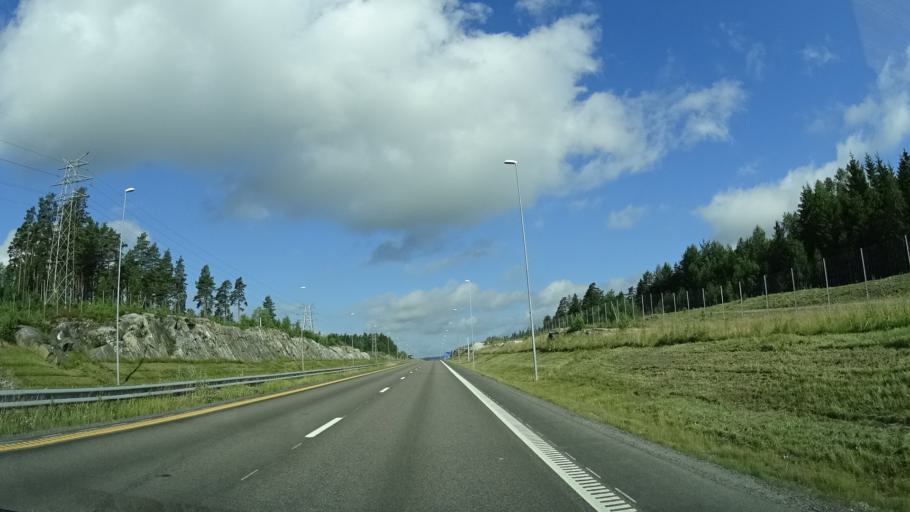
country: NO
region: Ostfold
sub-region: Hobol
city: Knappstad
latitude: 59.6109
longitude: 11.0252
